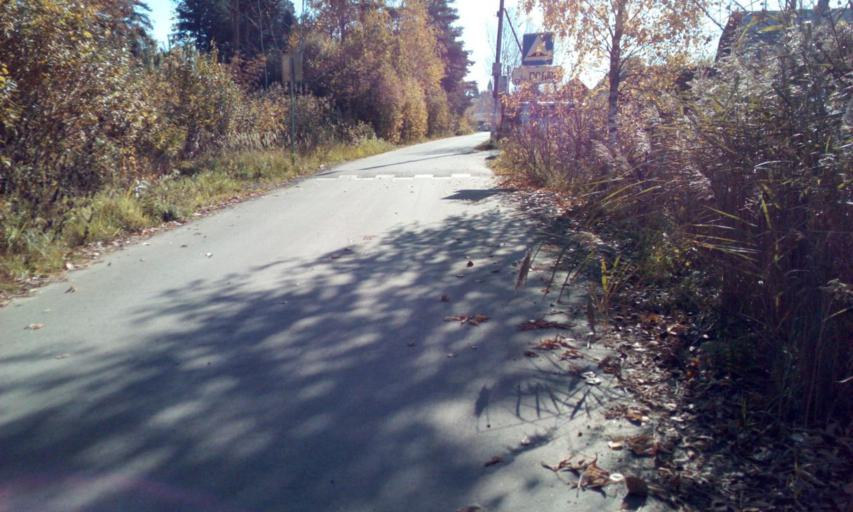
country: RU
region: Moskovskaya
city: Golitsyno
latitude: 55.5996
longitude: 36.9977
